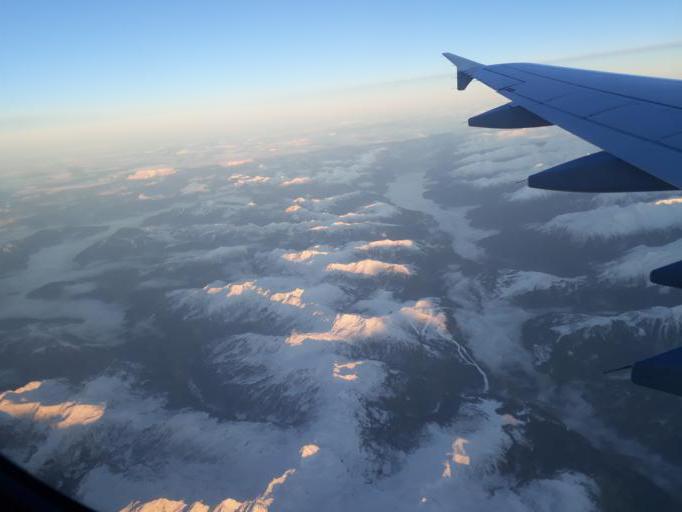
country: AT
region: Tyrol
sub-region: Politischer Bezirk Schwaz
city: Rohrberg
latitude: 47.2472
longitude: 11.9029
